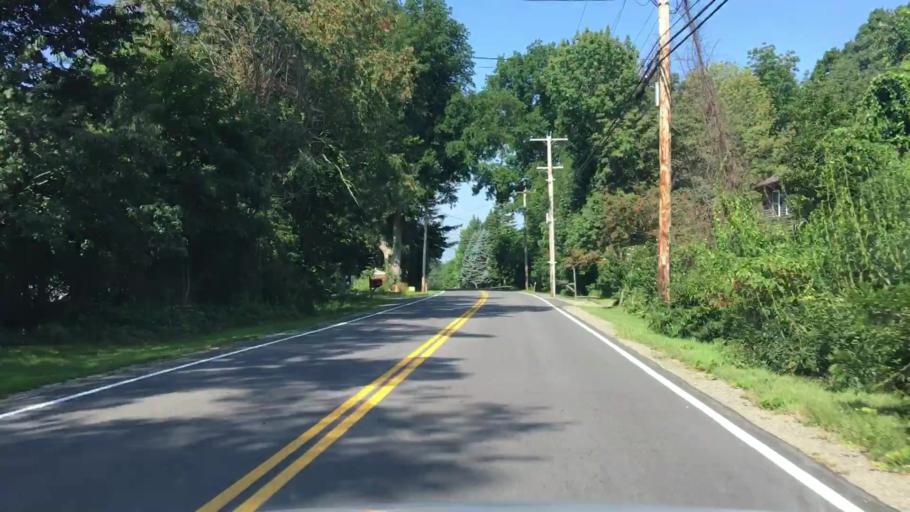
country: US
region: New Hampshire
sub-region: Rockingham County
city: East Kingston
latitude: 42.9222
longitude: -70.9970
